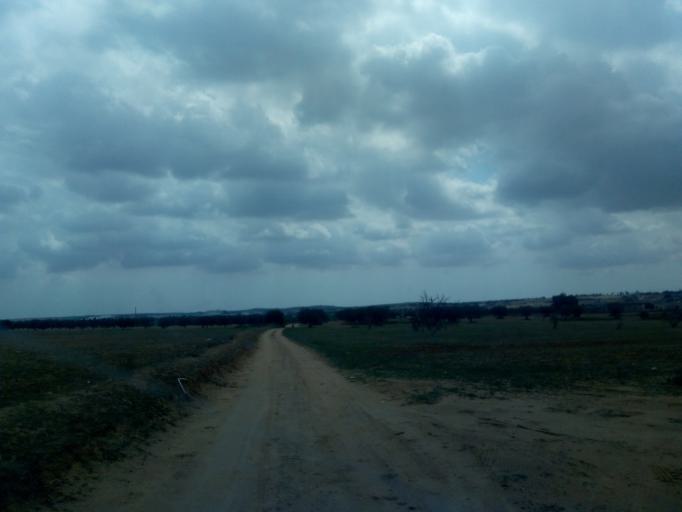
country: TN
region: Safaqis
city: Sfax
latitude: 34.7443
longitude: 10.4913
